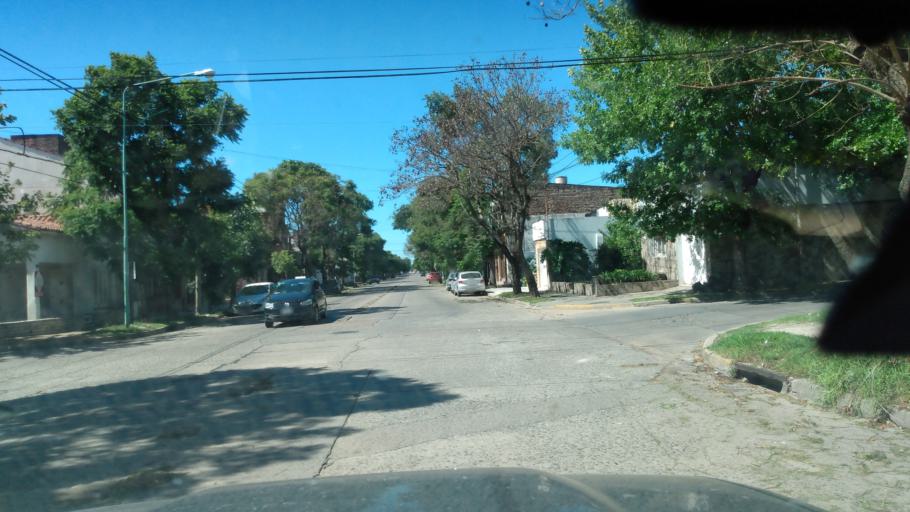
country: AR
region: Buenos Aires
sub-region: Partido de Lujan
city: Lujan
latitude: -34.5688
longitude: -59.1215
